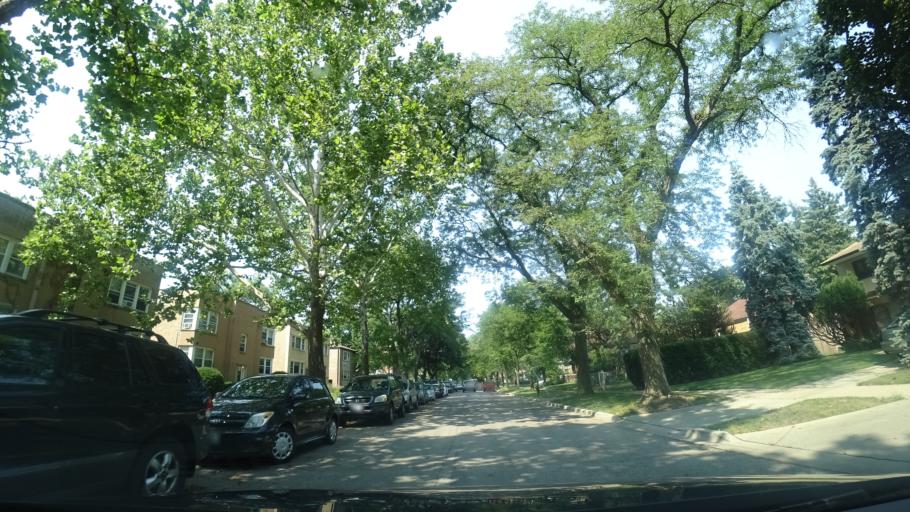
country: US
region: Illinois
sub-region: Cook County
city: Evanston
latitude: 42.0214
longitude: -87.6919
